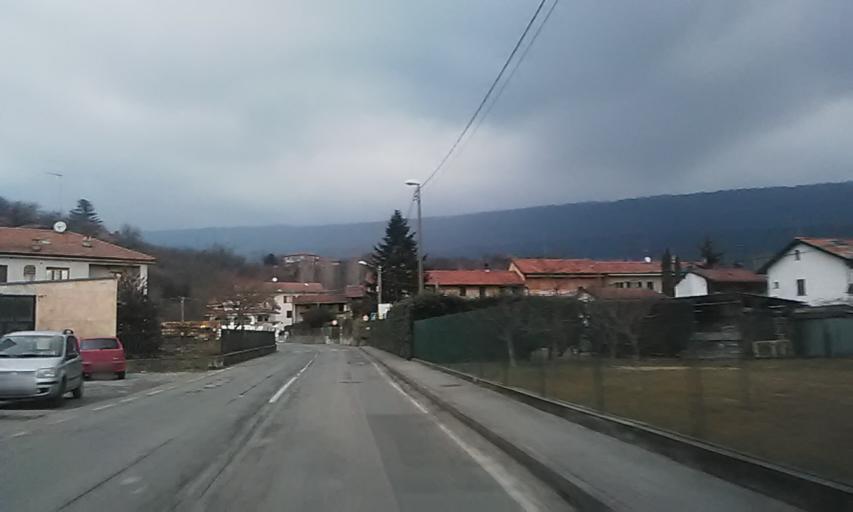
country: IT
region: Piedmont
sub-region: Provincia di Torino
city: Cascinette d'Ivrea
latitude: 45.4842
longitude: 7.9062
